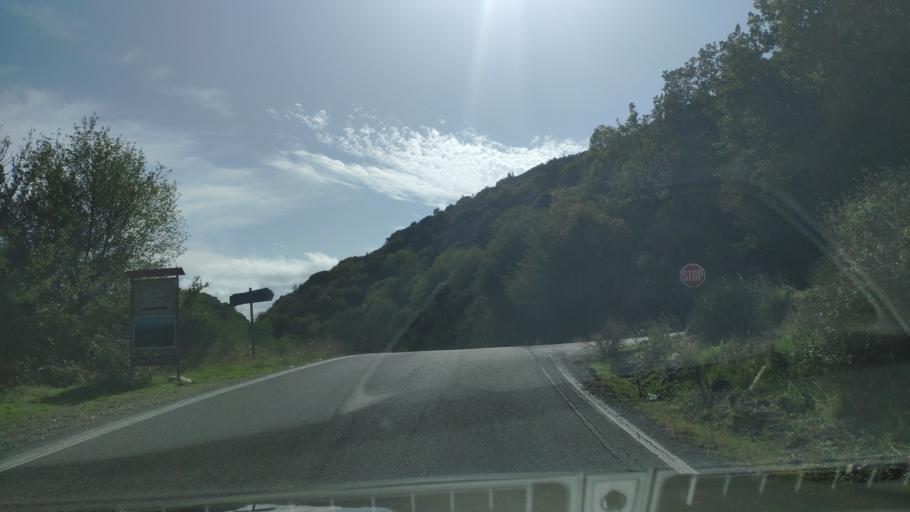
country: GR
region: Peloponnese
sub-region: Nomos Arkadias
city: Dimitsana
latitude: 37.5826
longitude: 22.0176
